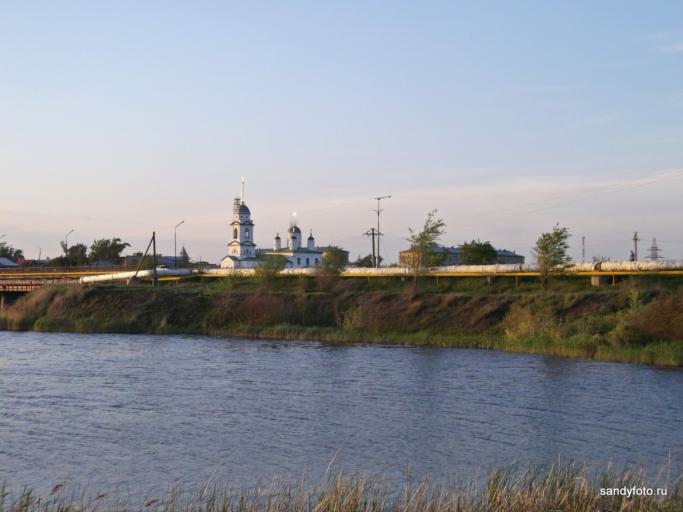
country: RU
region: Chelyabinsk
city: Troitsk
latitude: 54.0738
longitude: 61.5564
